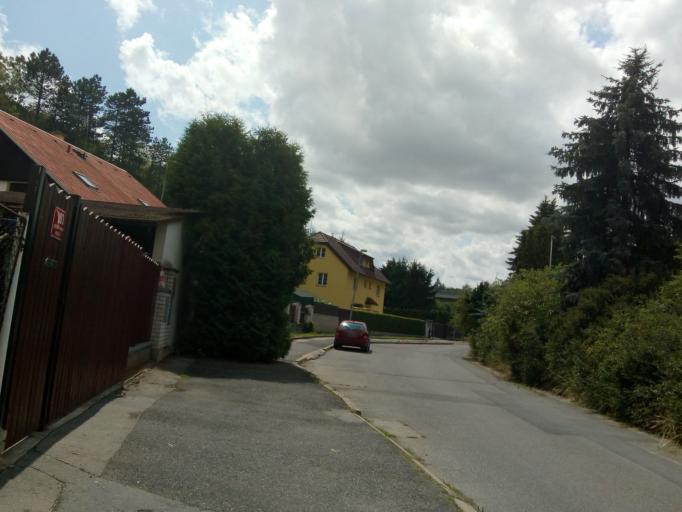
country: CZ
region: Central Bohemia
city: Tuchomerice
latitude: 50.1167
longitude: 14.2920
